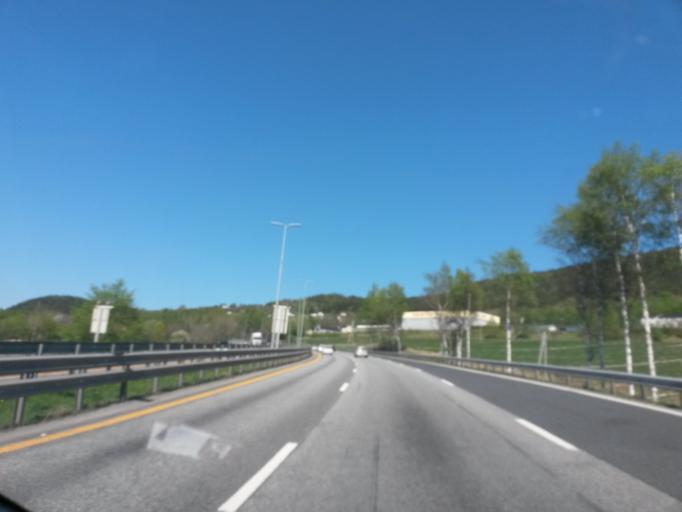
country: NO
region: Buskerud
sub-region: Lier
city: Lierbyen
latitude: 59.7759
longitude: 10.2762
